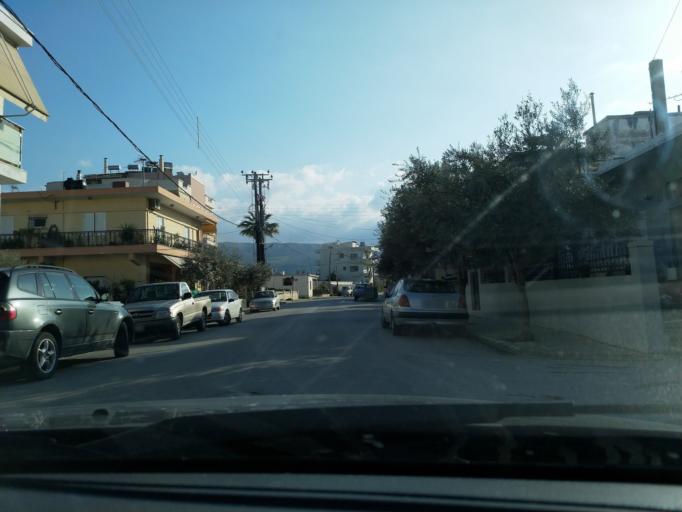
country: GR
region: Crete
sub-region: Nomos Chanias
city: Chania
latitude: 35.5017
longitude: 24.0254
